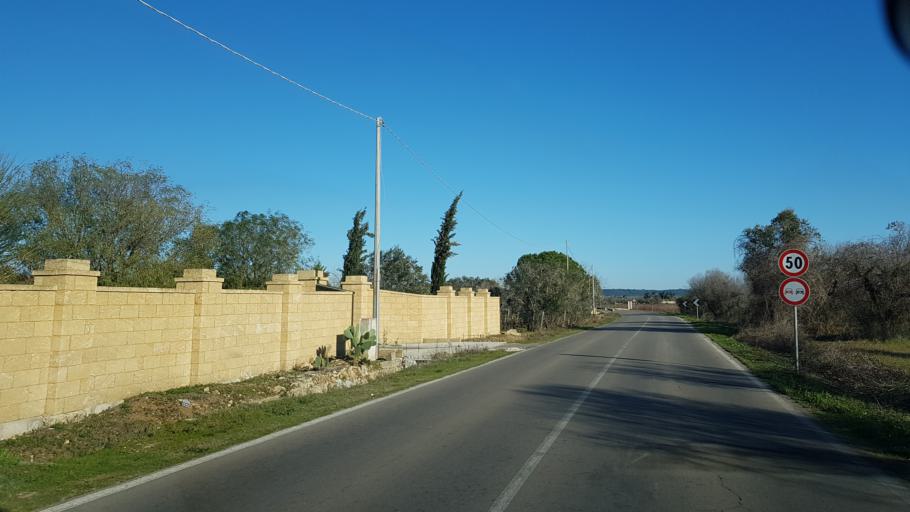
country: IT
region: Apulia
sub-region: Provincia di Lecce
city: Melissano
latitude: 39.9954
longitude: 18.1200
